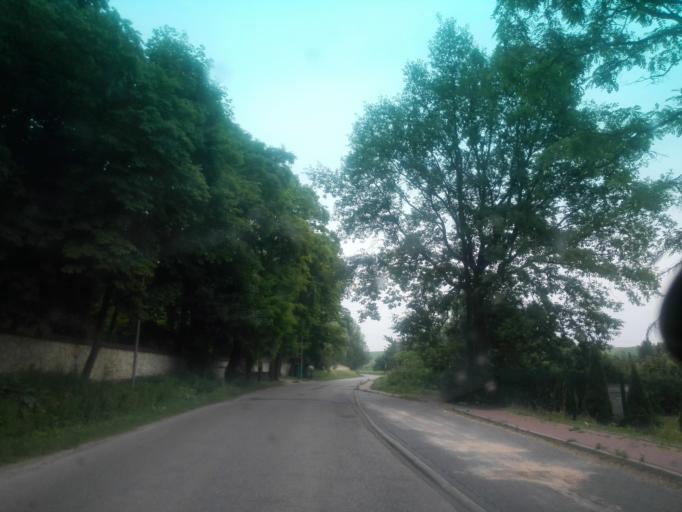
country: PL
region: Silesian Voivodeship
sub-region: Powiat czestochowski
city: Mstow
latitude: 50.7947
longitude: 19.3281
